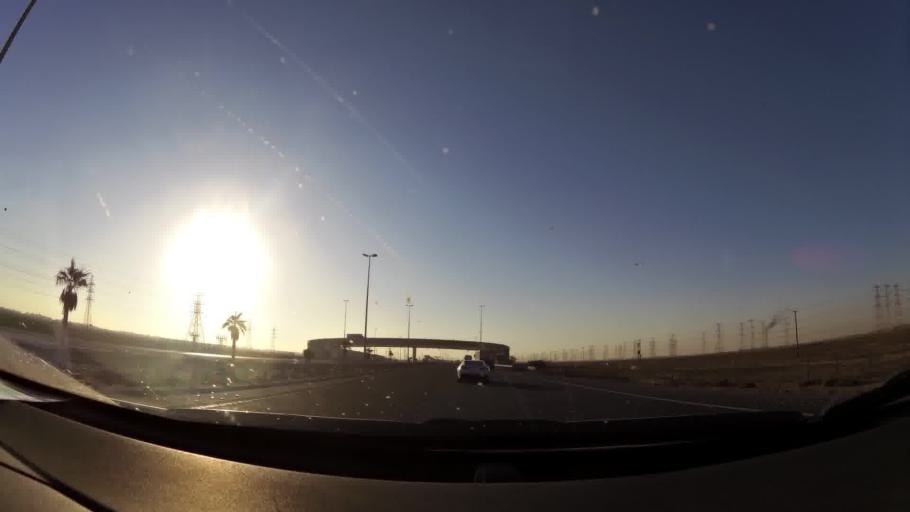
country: KW
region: Al Ahmadi
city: Al Fahahil
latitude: 28.8268
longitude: 48.2565
